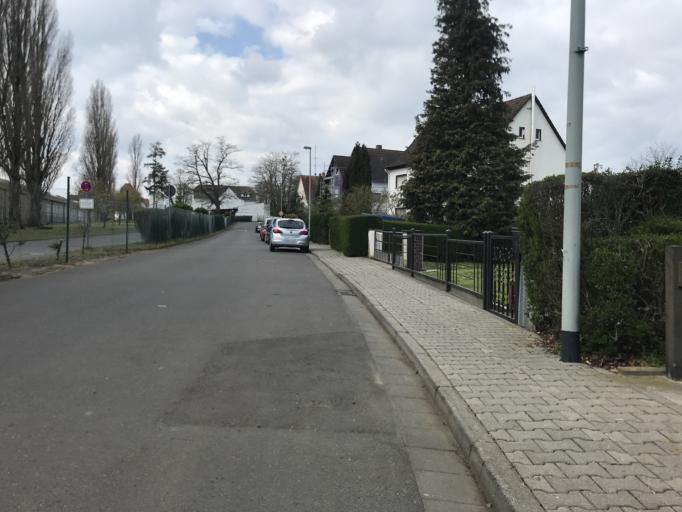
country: DE
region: Hesse
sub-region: Regierungsbezirk Darmstadt
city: Russelsheim
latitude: 50.0010
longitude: 8.4020
